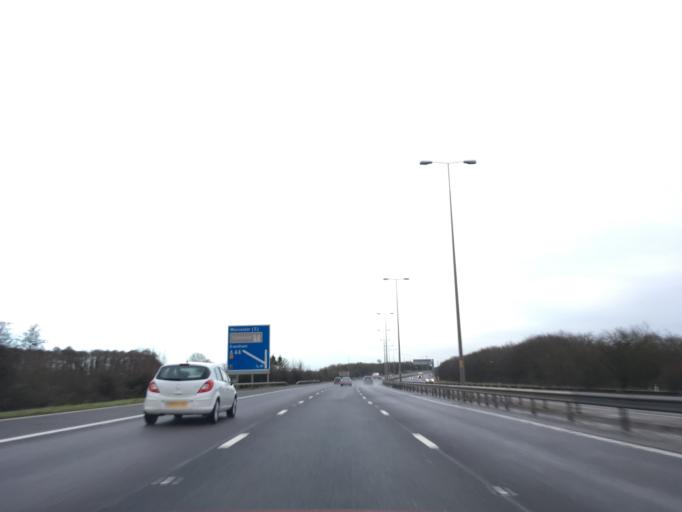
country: GB
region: England
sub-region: Worcestershire
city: Kempsey
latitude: 52.1558
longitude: -2.1905
